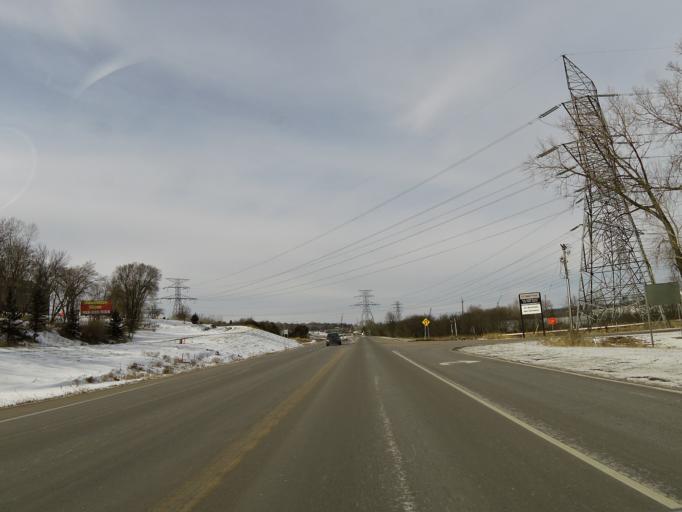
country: US
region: Minnesota
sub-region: Washington County
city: Bayport
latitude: 45.0282
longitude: -92.7848
